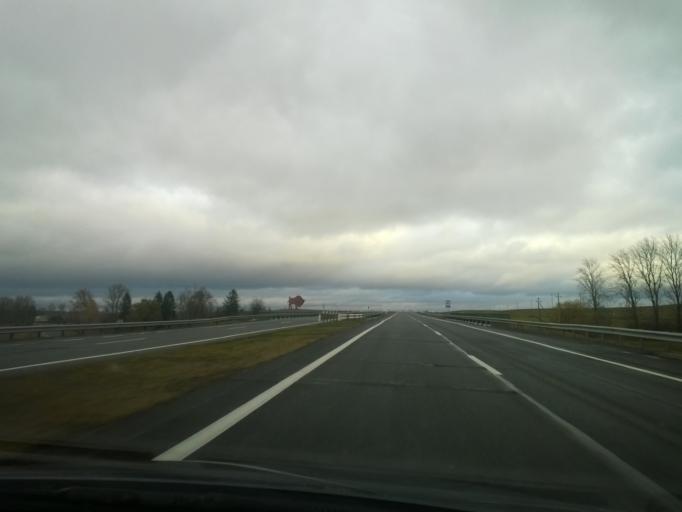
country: BY
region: Minsk
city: Snow
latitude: 53.2953
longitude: 26.3589
